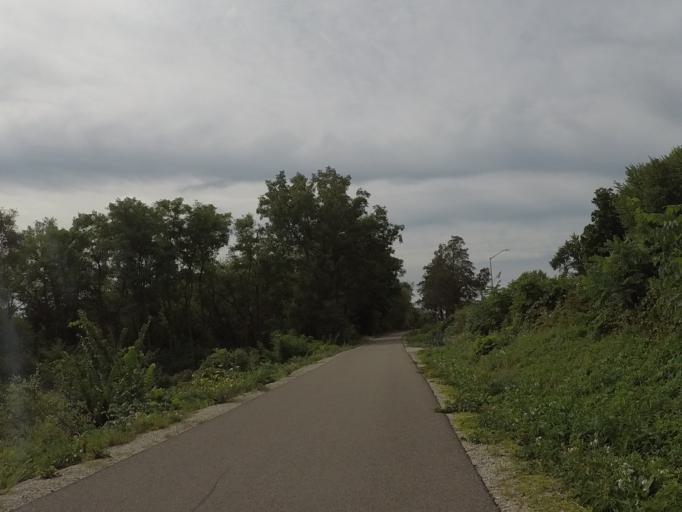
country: US
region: Wisconsin
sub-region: Sauk County
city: Prairie du Sac
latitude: 43.2854
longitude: -89.7178
